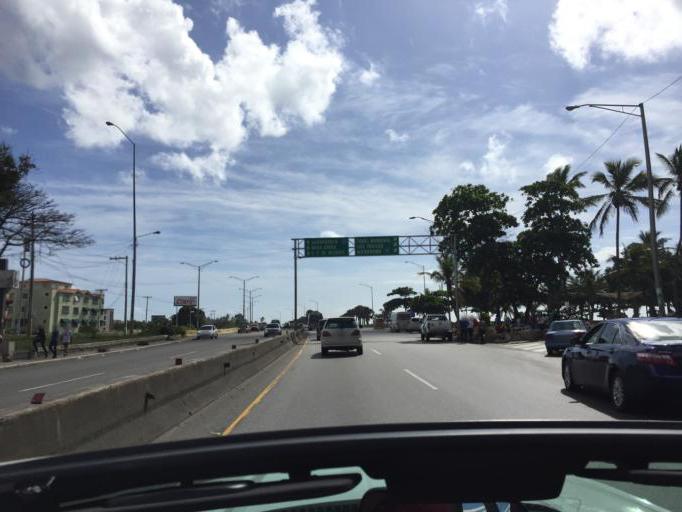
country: DO
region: Santo Domingo
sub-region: Santo Domingo
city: Santo Domingo Este
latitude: 18.4696
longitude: -69.8299
